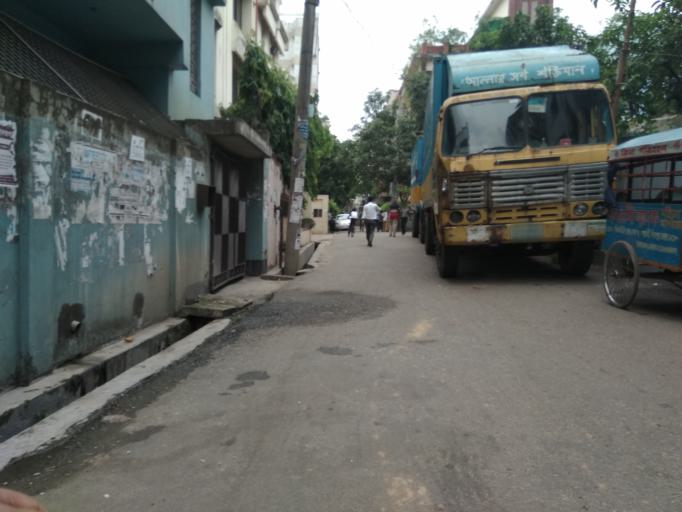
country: BD
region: Dhaka
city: Tungi
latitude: 23.8199
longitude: 90.3614
